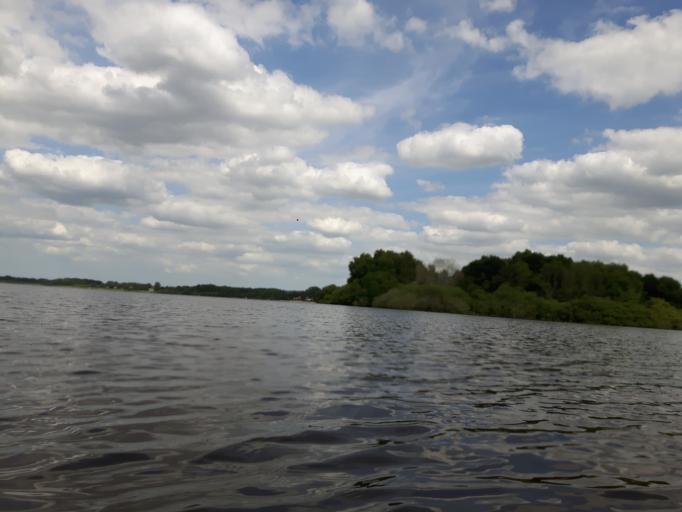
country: DE
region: Schleswig-Holstein
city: Muhbrook
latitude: 54.1334
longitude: 9.9946
